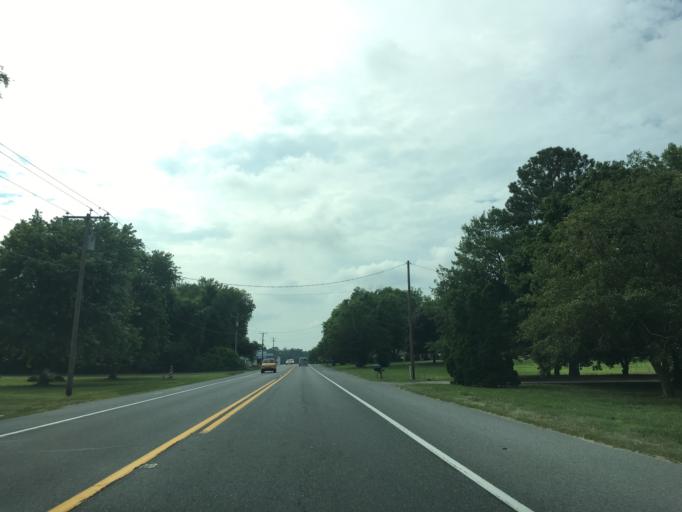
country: US
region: Delaware
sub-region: Sussex County
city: Long Neck
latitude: 38.5547
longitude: -75.1953
